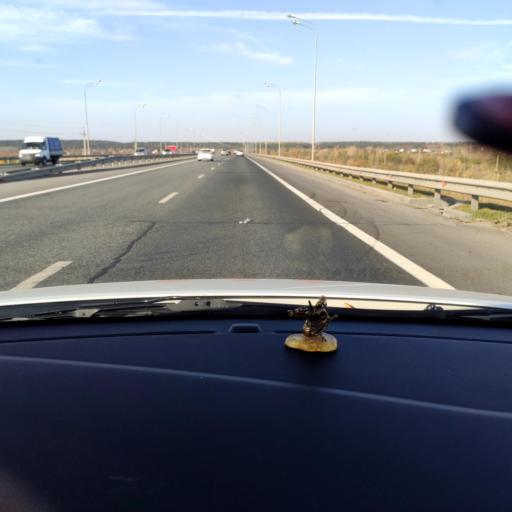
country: RU
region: Tatarstan
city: Osinovo
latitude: 55.8067
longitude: 48.8418
